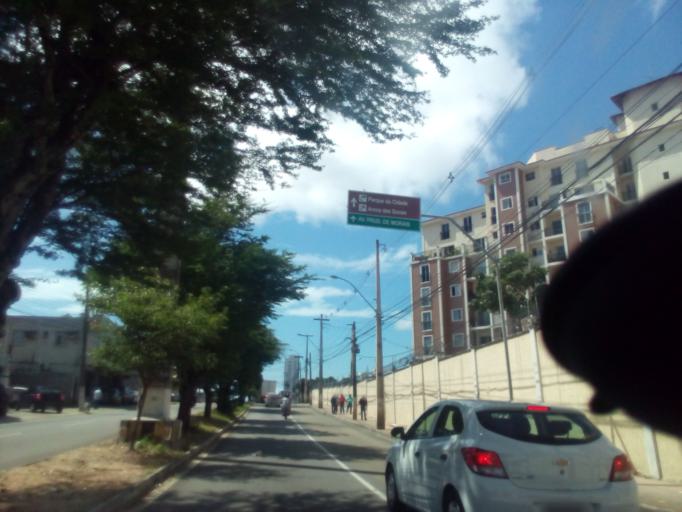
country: BR
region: Rio Grande do Norte
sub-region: Natal
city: Natal
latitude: -5.8232
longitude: -35.2281
